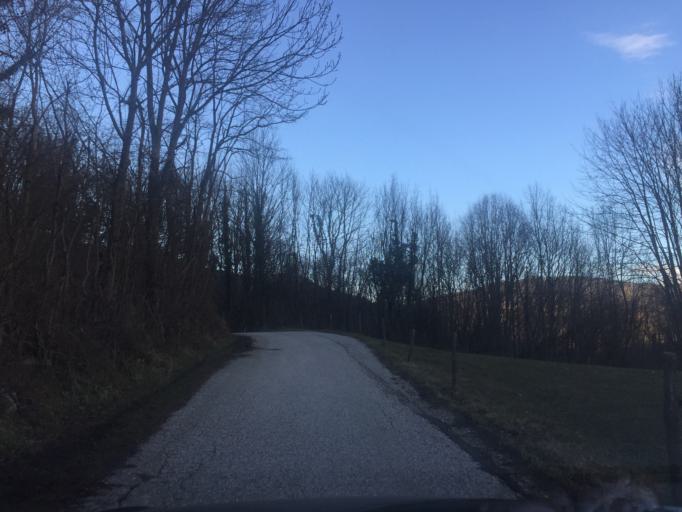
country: SI
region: Kanal
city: Deskle
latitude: 46.0357
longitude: 13.6650
